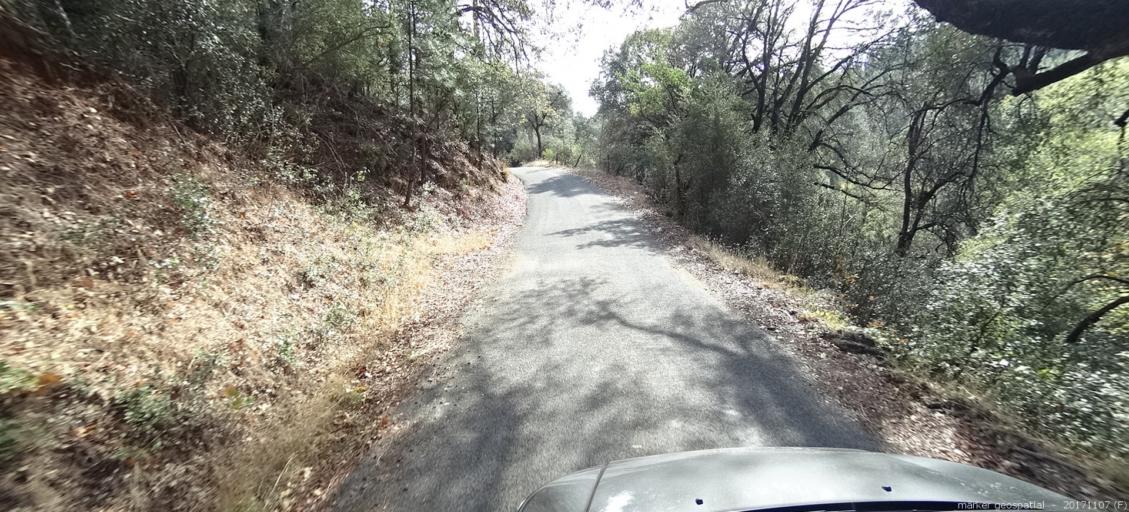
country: US
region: California
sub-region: Shasta County
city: Shasta
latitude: 40.5407
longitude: -122.5677
